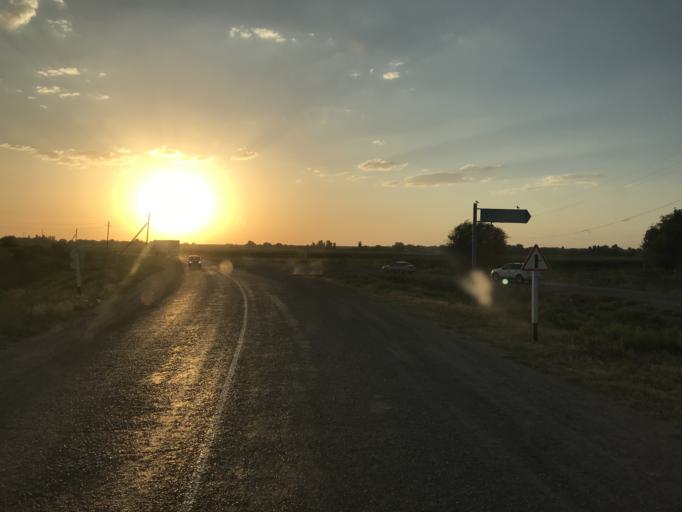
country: UZ
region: Toshkent
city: Yangiyul
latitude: 41.3749
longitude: 68.8255
